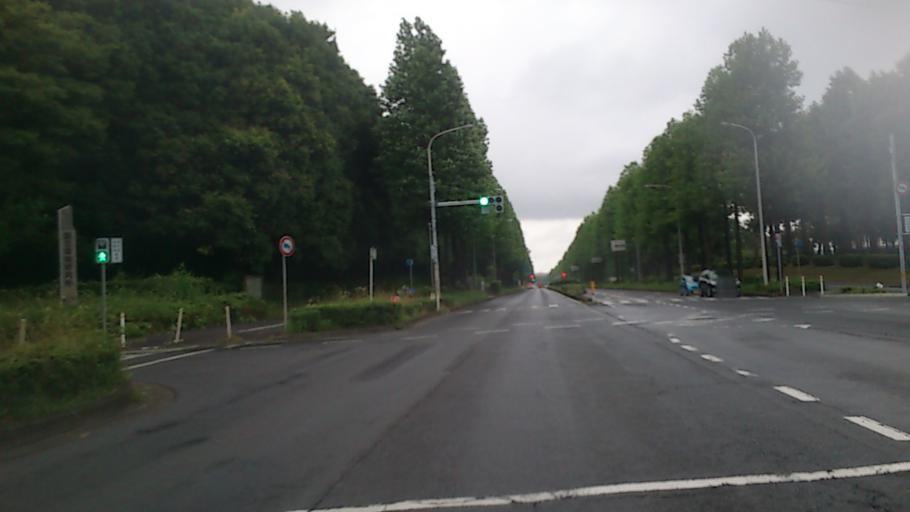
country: JP
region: Ibaraki
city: Naka
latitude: 36.0503
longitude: 140.1223
